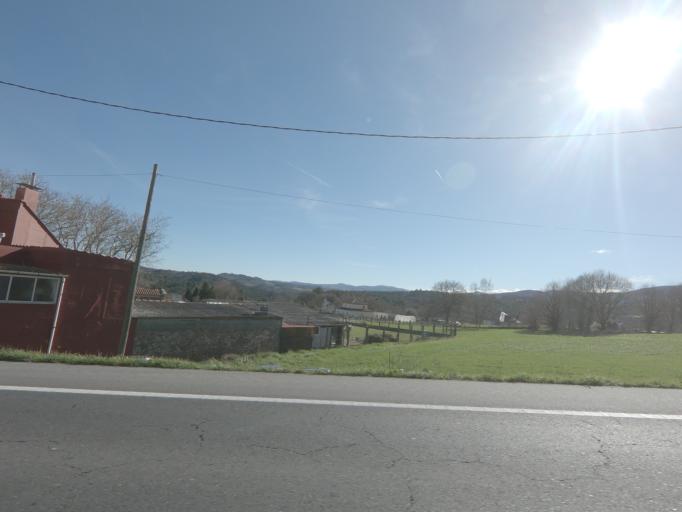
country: ES
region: Galicia
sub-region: Provincia de Pontevedra
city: Silleda
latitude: 42.6861
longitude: -8.2148
